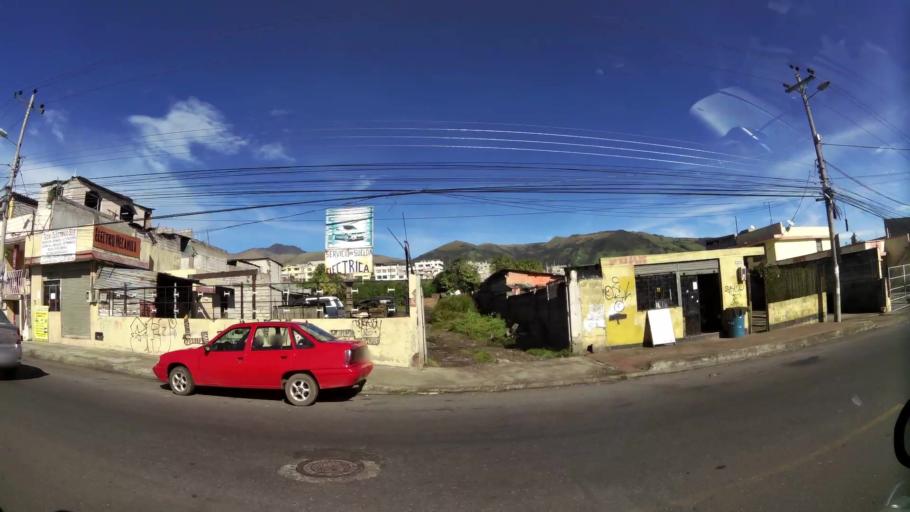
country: EC
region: Pichincha
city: Sangolqui
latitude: -0.3308
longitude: -78.5551
